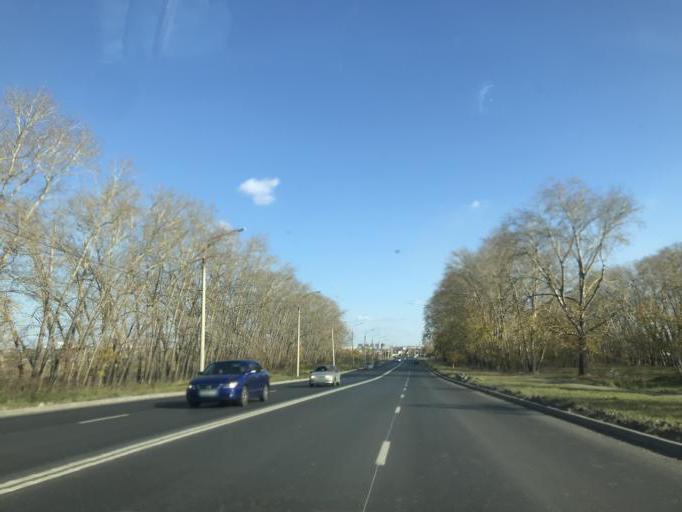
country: RU
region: Chelyabinsk
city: Roshchino
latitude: 55.2401
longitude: 61.3366
